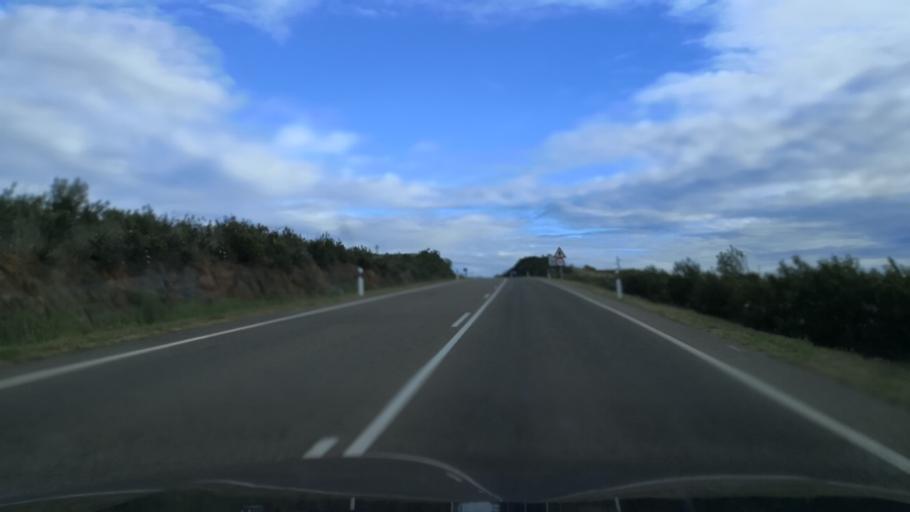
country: ES
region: Extremadura
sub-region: Provincia de Caceres
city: Torrejoncillo
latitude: 39.9335
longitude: -6.5054
